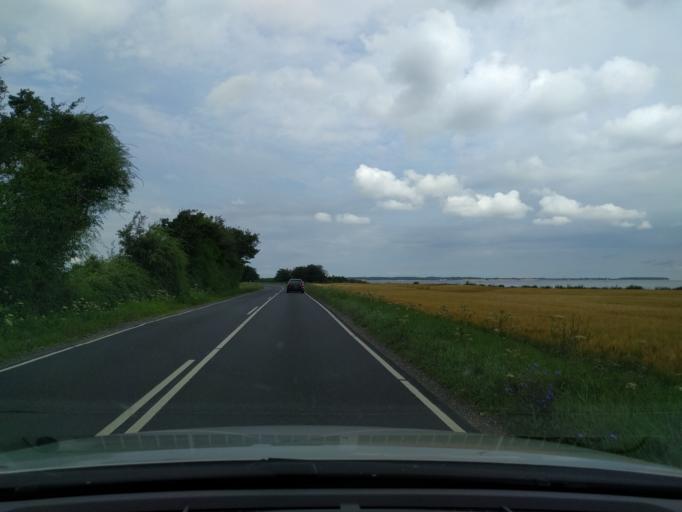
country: DK
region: South Denmark
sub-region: Kerteminde Kommune
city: Kerteminde
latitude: 55.4189
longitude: 10.7081
